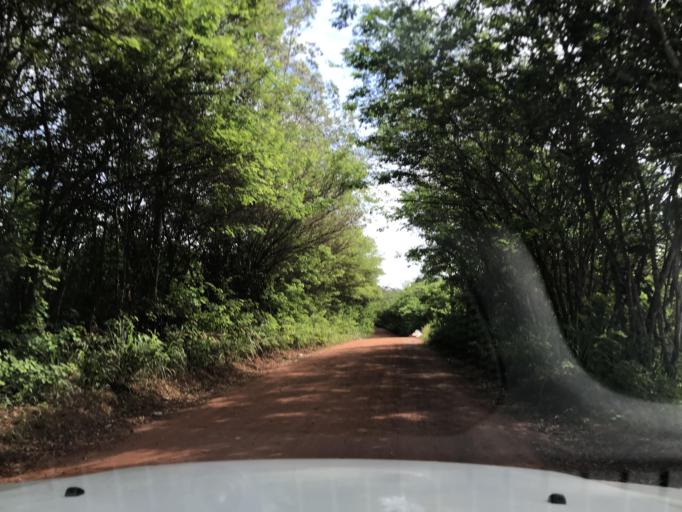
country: BR
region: Bahia
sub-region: Entre Rios
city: Entre Rios
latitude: -12.1780
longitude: -38.1219
